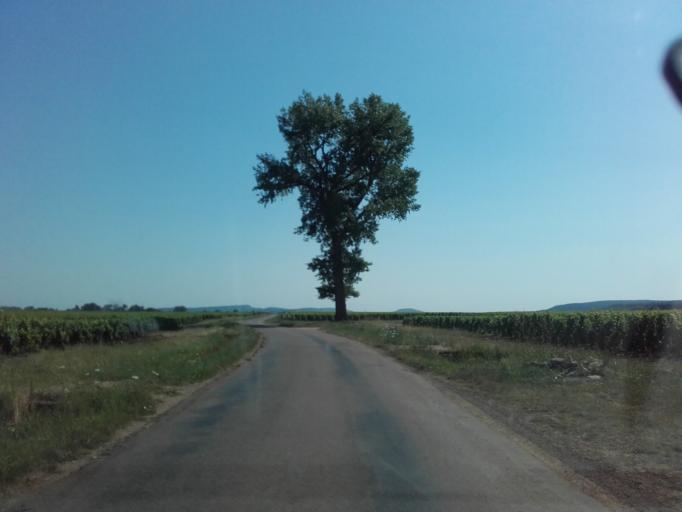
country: FR
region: Bourgogne
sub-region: Departement de la Cote-d'Or
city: Meursault
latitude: 46.9613
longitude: 4.7599
